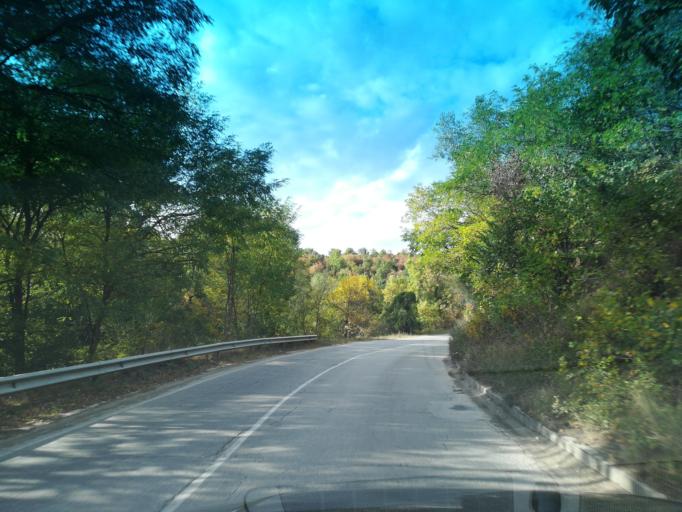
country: BG
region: Pazardzhik
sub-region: Obshtina Peshtera
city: Peshtera
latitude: 42.0511
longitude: 24.3391
